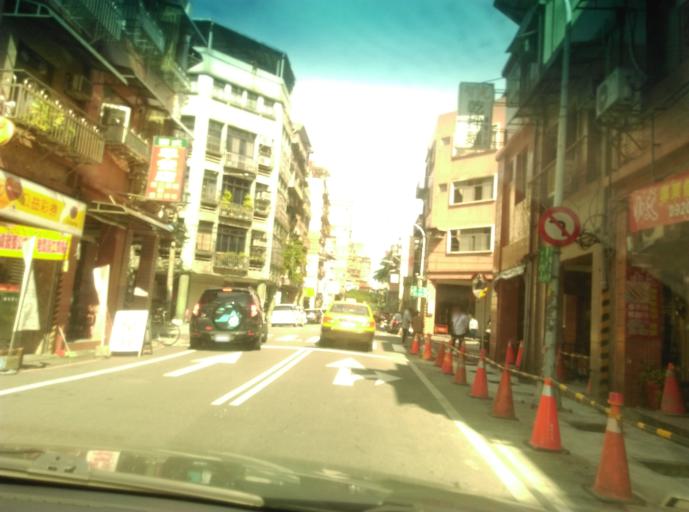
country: TW
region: Taiwan
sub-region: Keelung
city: Keelung
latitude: 25.1348
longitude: 121.7479
